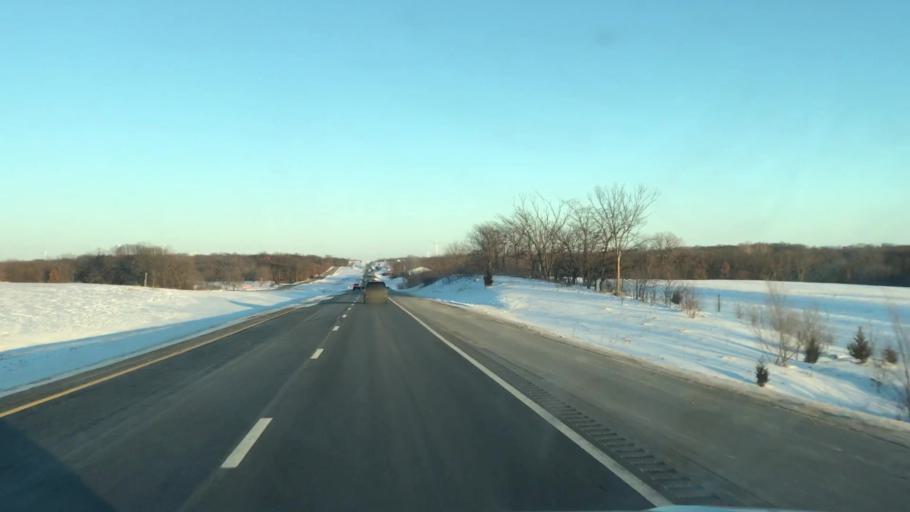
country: US
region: Missouri
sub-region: DeKalb County
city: Maysville
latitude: 39.7620
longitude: -94.4910
